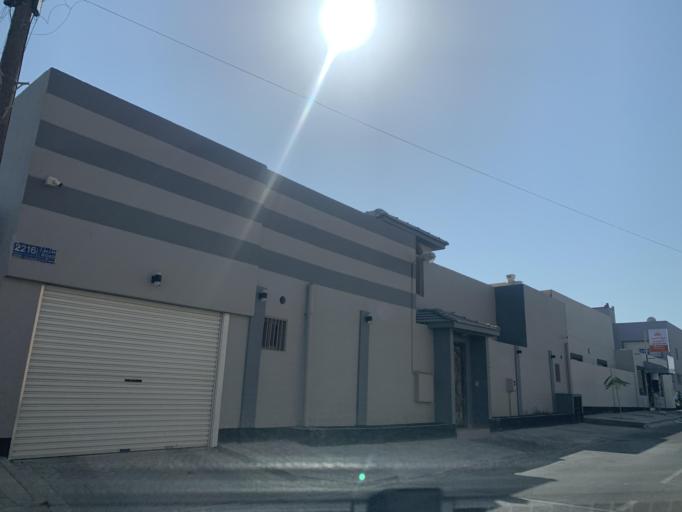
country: BH
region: Central Governorate
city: Madinat Hamad
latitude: 26.1258
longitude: 50.4798
